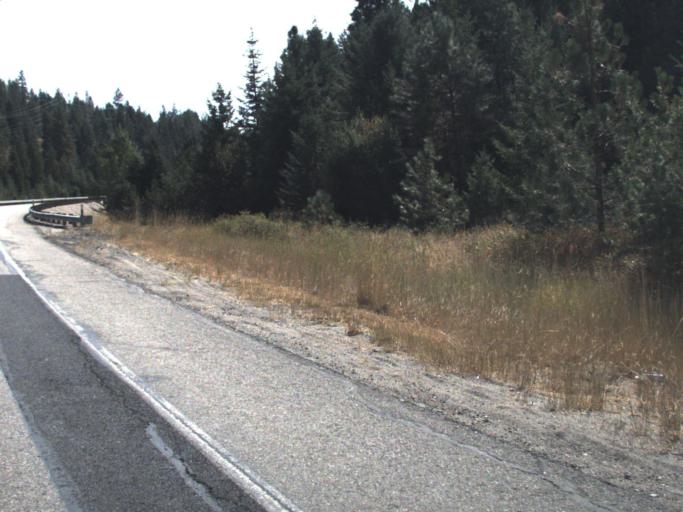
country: US
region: Washington
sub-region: Stevens County
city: Chewelah
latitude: 48.1415
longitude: -117.6599
